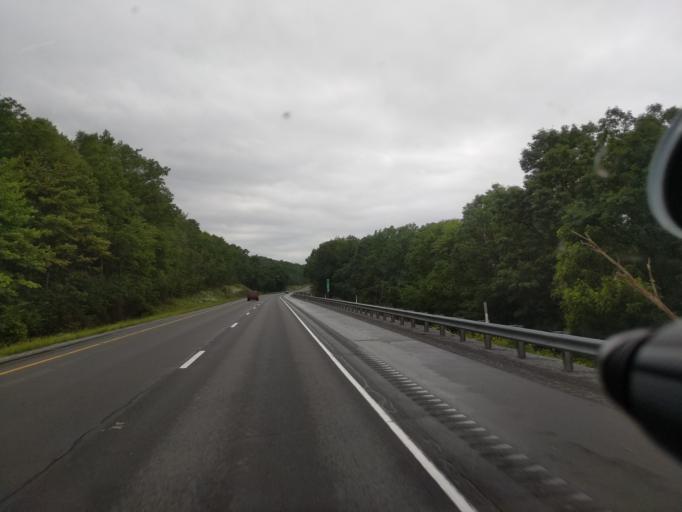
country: US
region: Pennsylvania
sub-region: Clinton County
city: Avis
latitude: 41.0609
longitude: -77.2439
